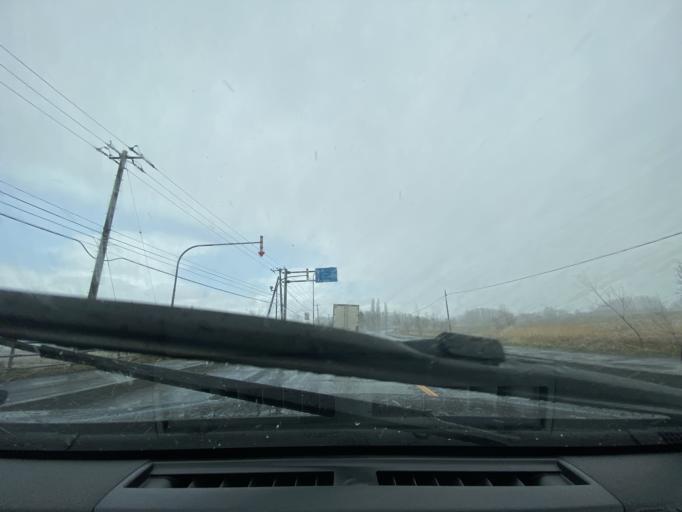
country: JP
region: Hokkaido
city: Takikawa
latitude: 43.6403
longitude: 141.9484
